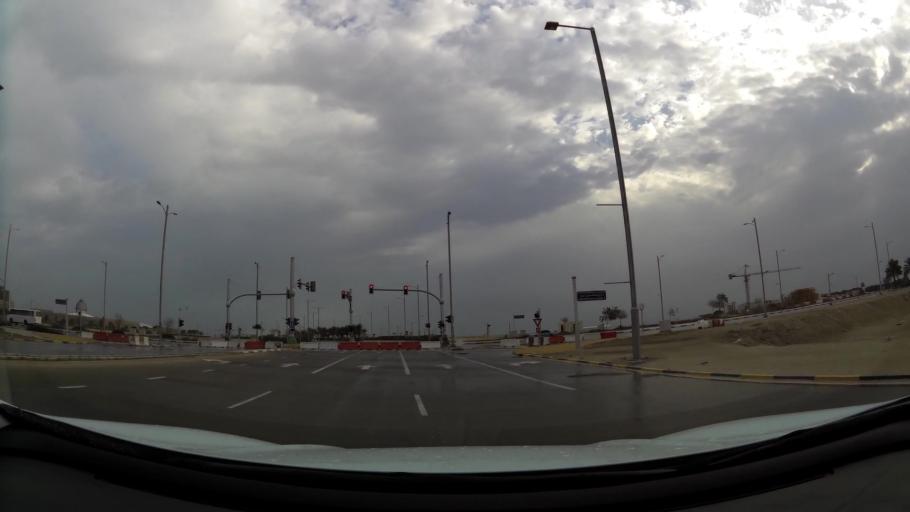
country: AE
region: Abu Dhabi
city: Abu Dhabi
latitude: 24.4828
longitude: 54.4118
